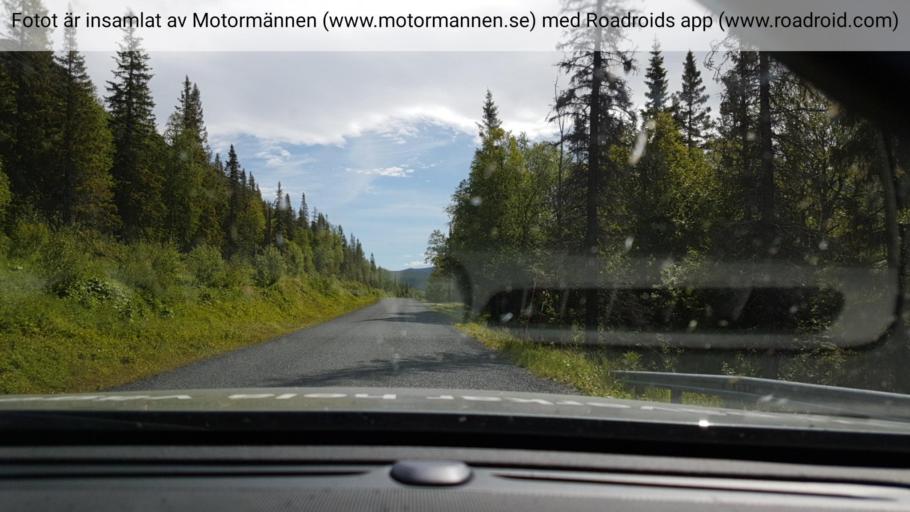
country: SE
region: Vaesterbotten
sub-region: Vilhelmina Kommun
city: Sjoberg
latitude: 65.2434
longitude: 15.4334
